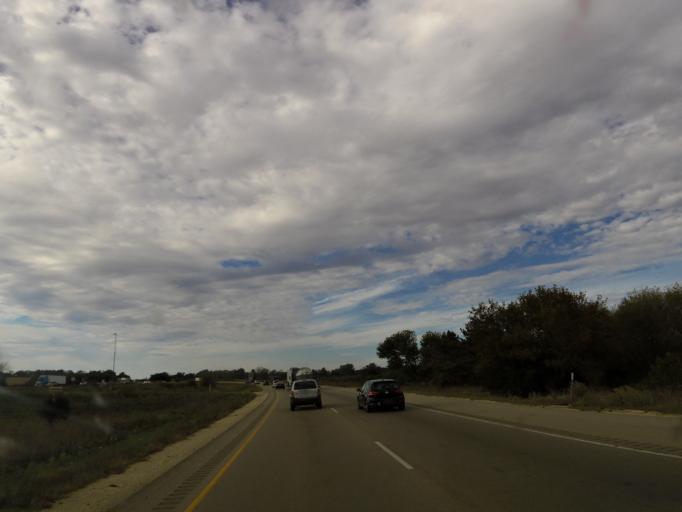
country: US
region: Wisconsin
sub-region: Rock County
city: Milton
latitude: 42.8008
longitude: -89.0049
